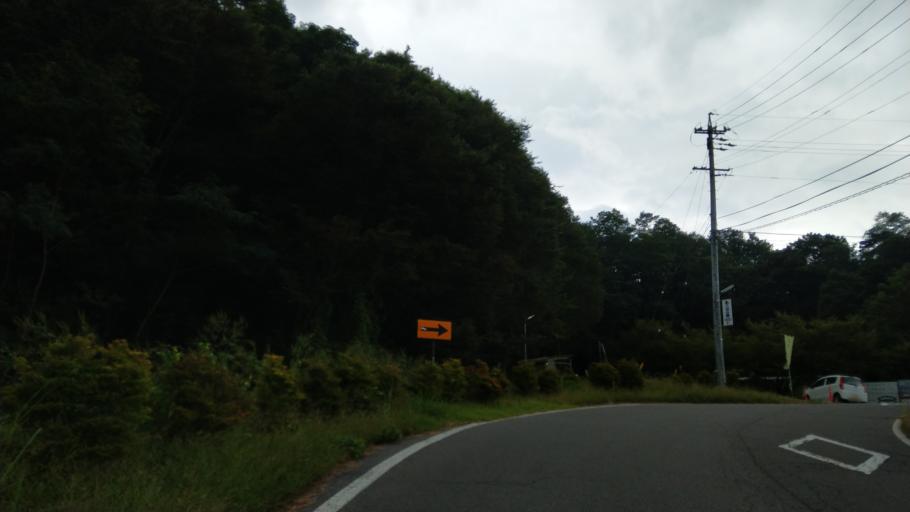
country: JP
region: Nagano
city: Komoro
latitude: 36.3276
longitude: 138.4002
